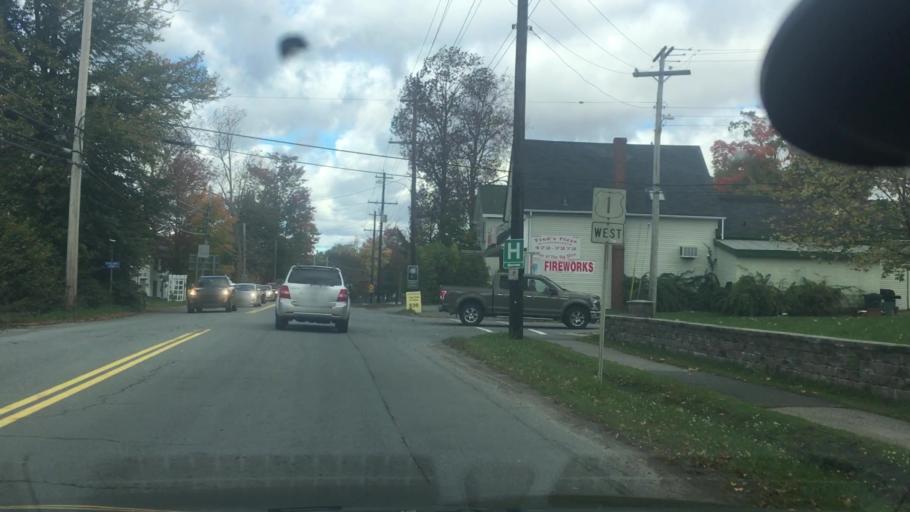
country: CA
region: Nova Scotia
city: Windsor
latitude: 44.9800
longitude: -64.1291
